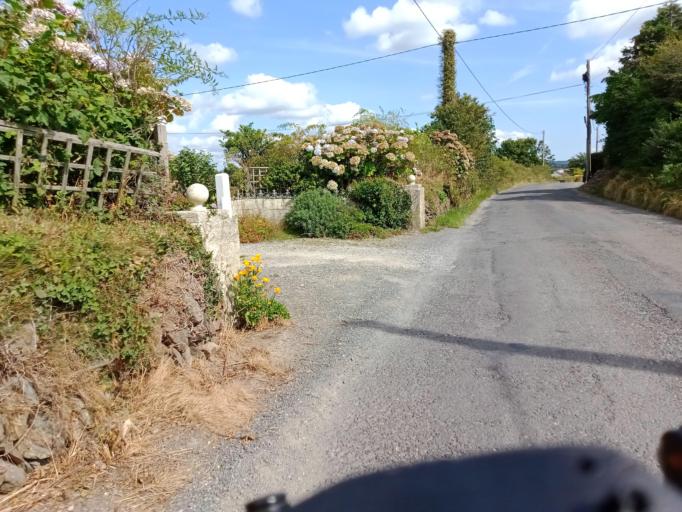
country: IE
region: Munster
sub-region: Waterford
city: Dungarvan
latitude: 52.1193
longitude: -7.4894
